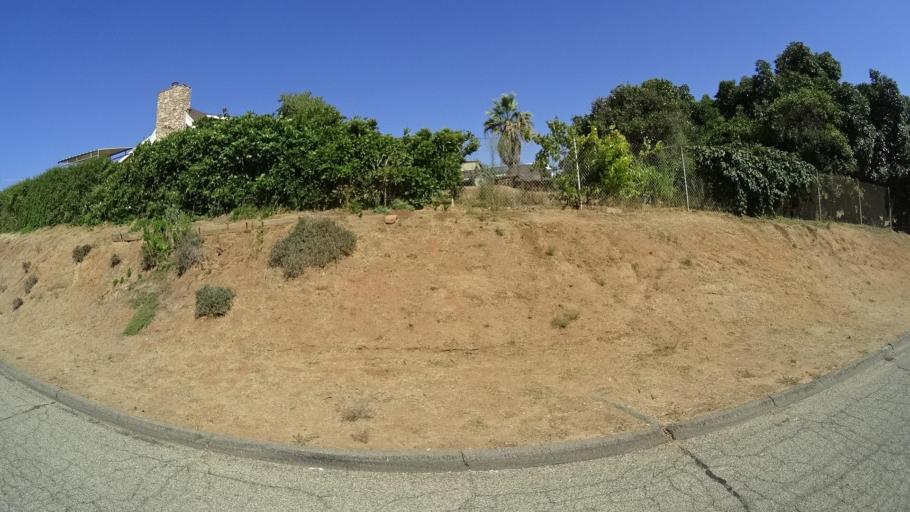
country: US
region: California
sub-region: San Diego County
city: Bonsall
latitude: 33.2881
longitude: -117.1959
